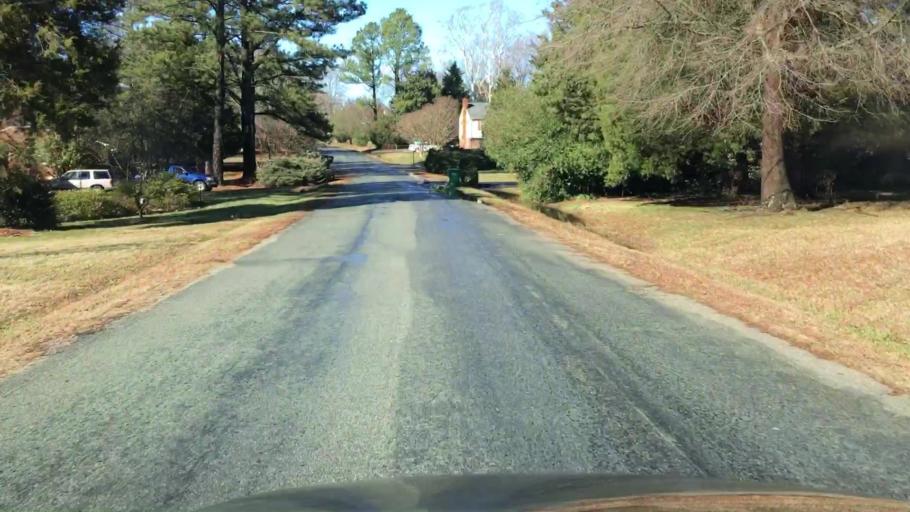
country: US
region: Virginia
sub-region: Chesterfield County
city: Bon Air
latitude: 37.5289
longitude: -77.5906
